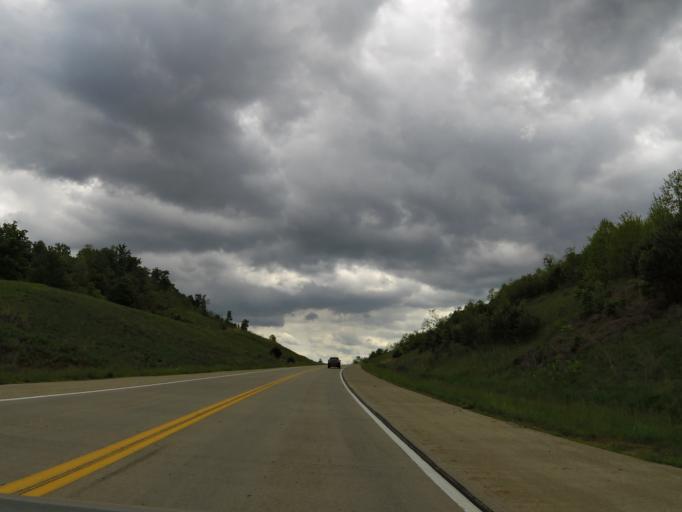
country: US
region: West Virginia
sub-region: Jackson County
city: Ravenswood
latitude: 38.9609
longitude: -81.8212
